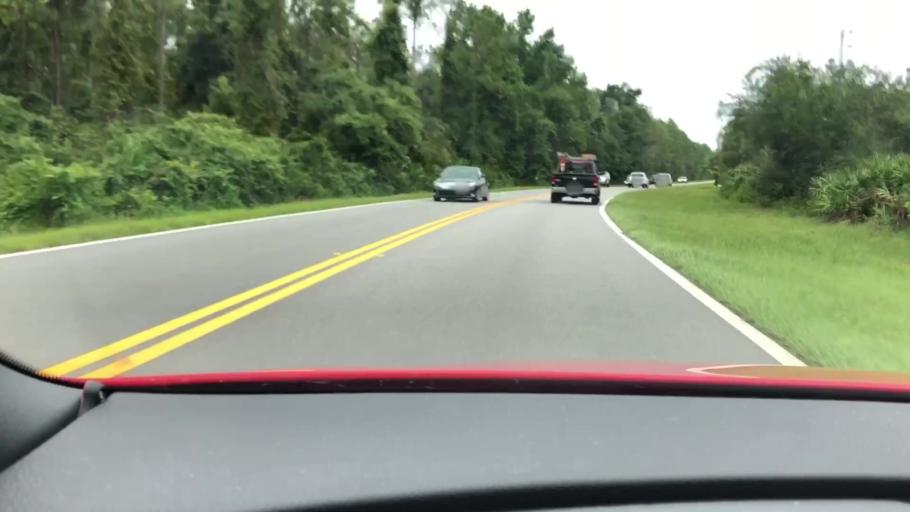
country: US
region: Florida
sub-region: Flagler County
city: Palm Coast
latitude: 29.5367
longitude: -81.2050
